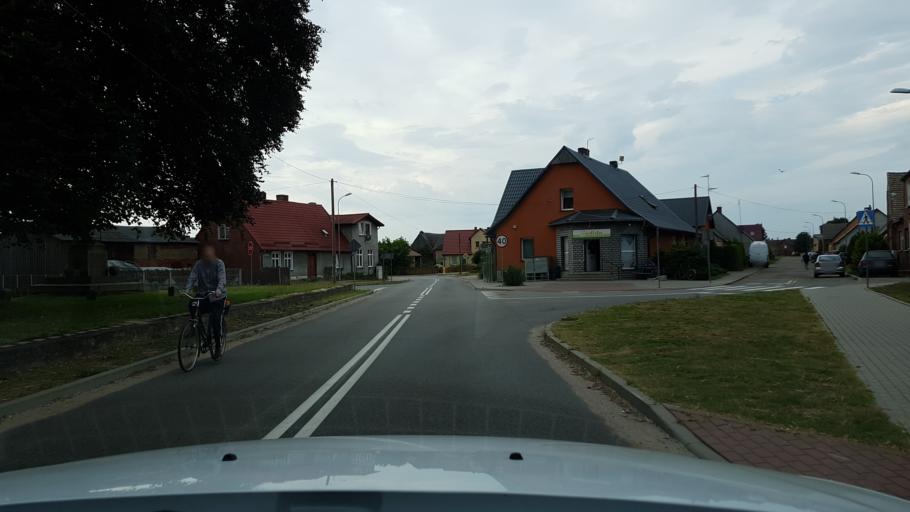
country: PL
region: West Pomeranian Voivodeship
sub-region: Powiat drawski
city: Wierzchowo
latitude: 53.4610
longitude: 16.1019
